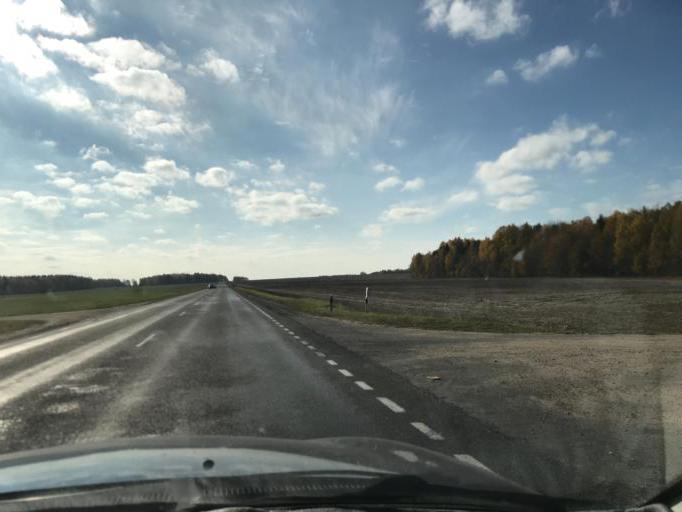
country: BY
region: Grodnenskaya
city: Voranava
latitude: 54.2014
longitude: 25.3480
